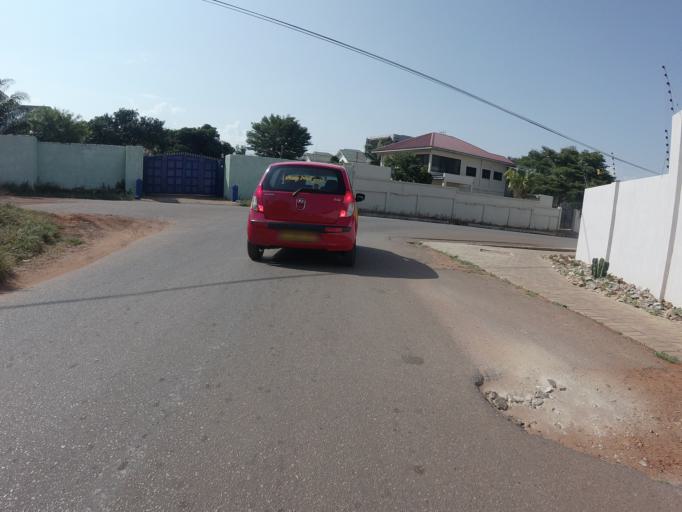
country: GH
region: Greater Accra
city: Accra
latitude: 5.5773
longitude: -0.1603
